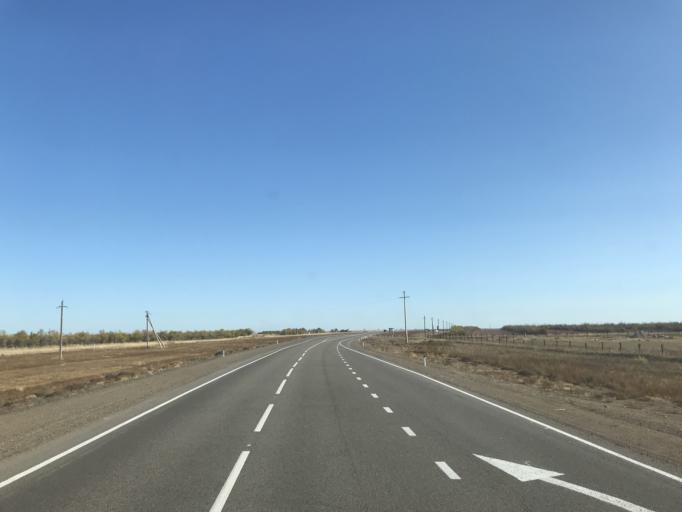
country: KZ
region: Pavlodar
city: Koktobe
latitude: 51.9023
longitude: 77.3822
